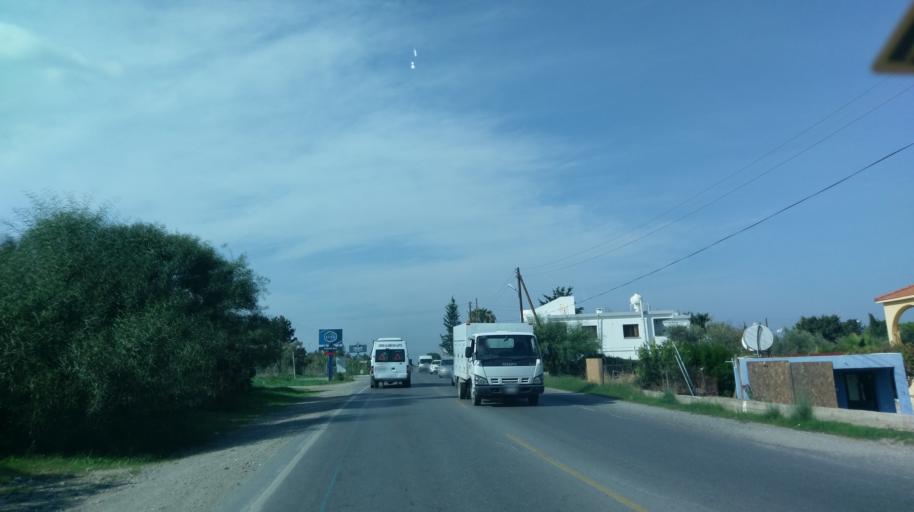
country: CY
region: Keryneia
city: Lapithos
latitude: 35.3431
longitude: 33.2439
